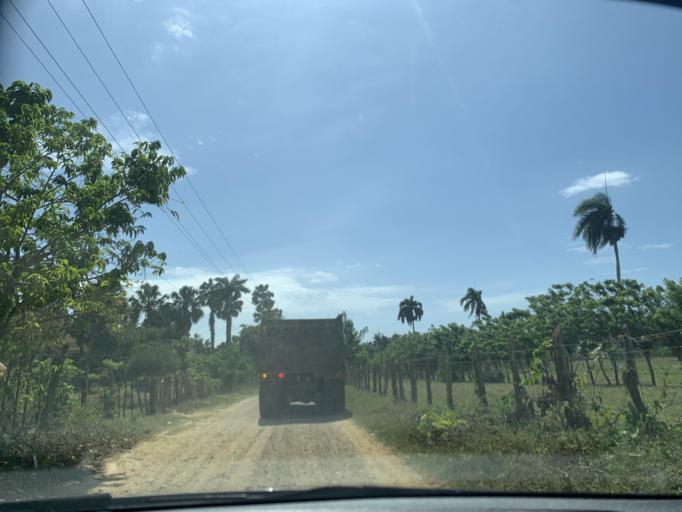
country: DO
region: Puerto Plata
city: Luperon
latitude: 19.8897
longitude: -70.8783
